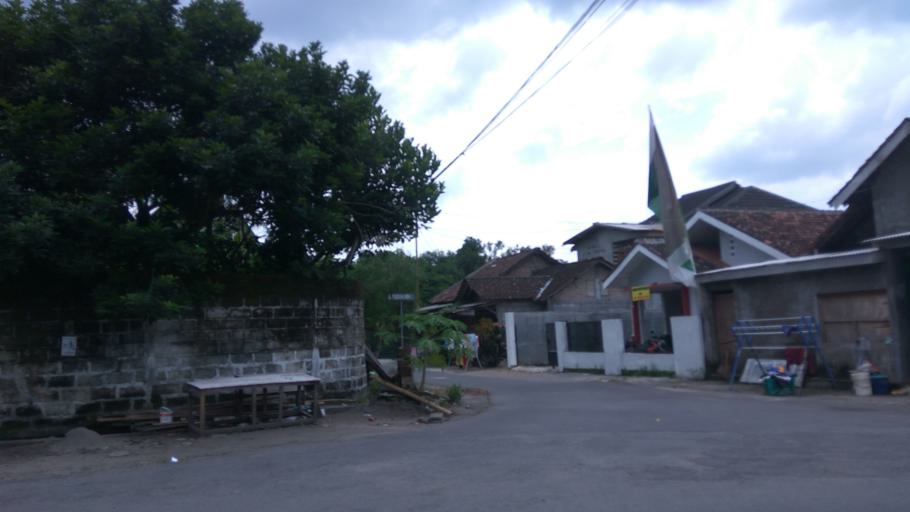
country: ID
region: Daerah Istimewa Yogyakarta
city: Melati
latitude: -7.7328
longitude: 110.4032
